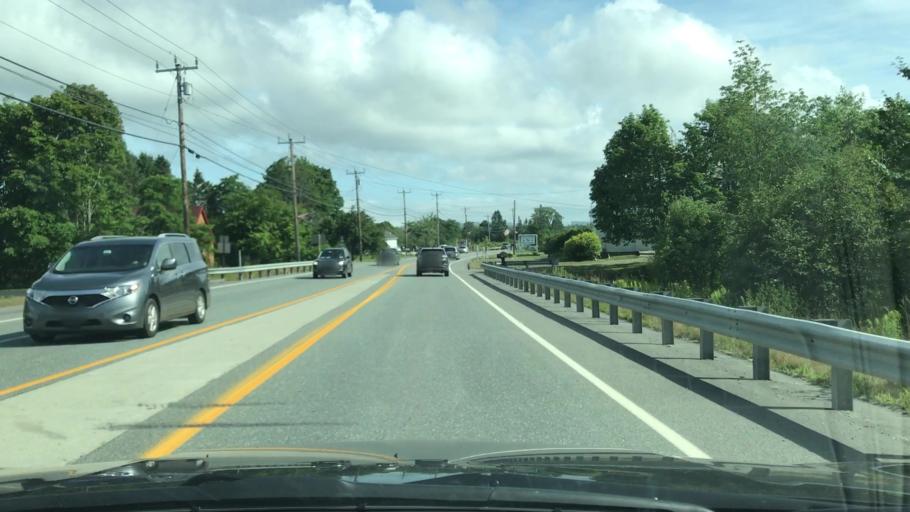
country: US
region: Maine
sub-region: Hancock County
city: Trenton
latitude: 44.4378
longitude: -68.3697
